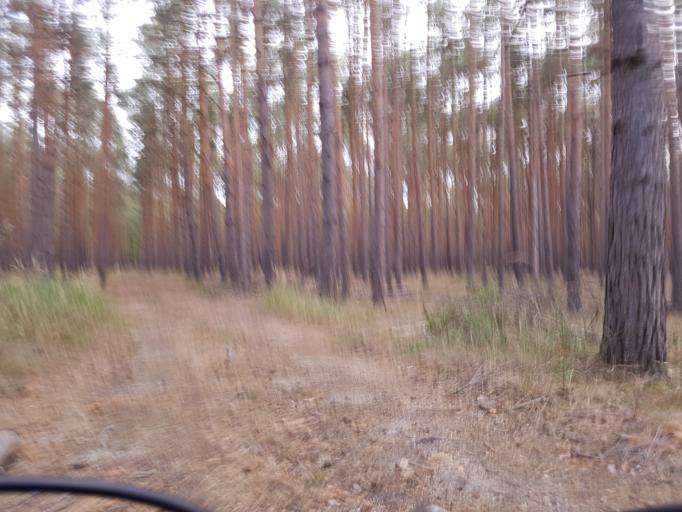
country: DE
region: Brandenburg
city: Trobitz
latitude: 51.5688
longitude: 13.4325
